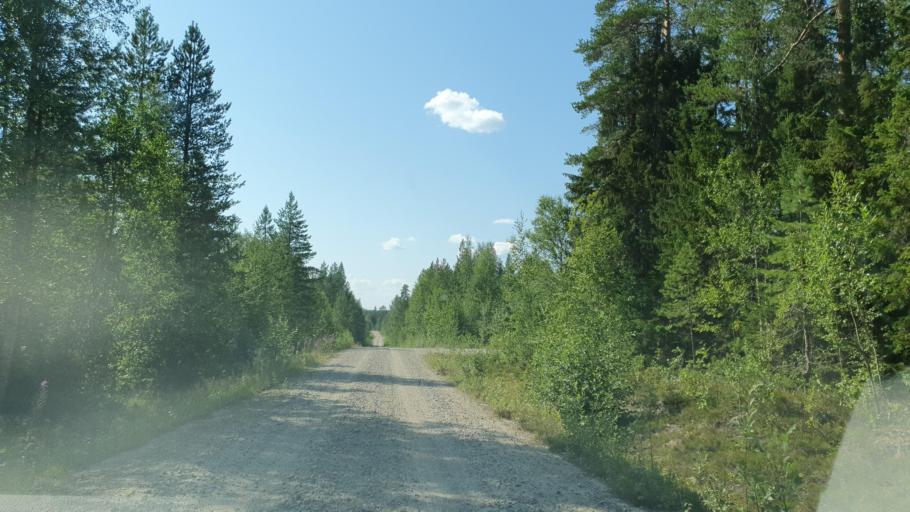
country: FI
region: Kainuu
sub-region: Kehys-Kainuu
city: Kuhmo
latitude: 64.0092
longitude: 29.5716
